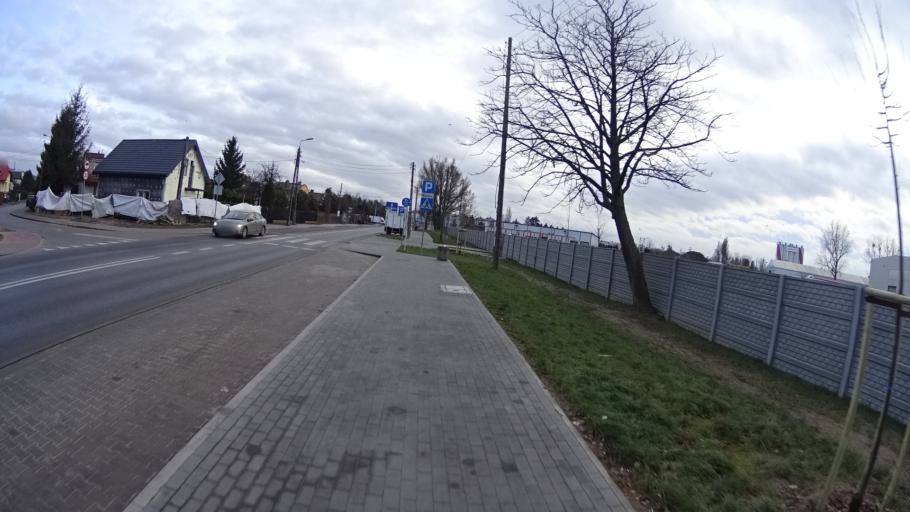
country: PL
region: Masovian Voivodeship
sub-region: Powiat pruszkowski
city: Pruszkow
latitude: 52.1651
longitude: 20.7781
